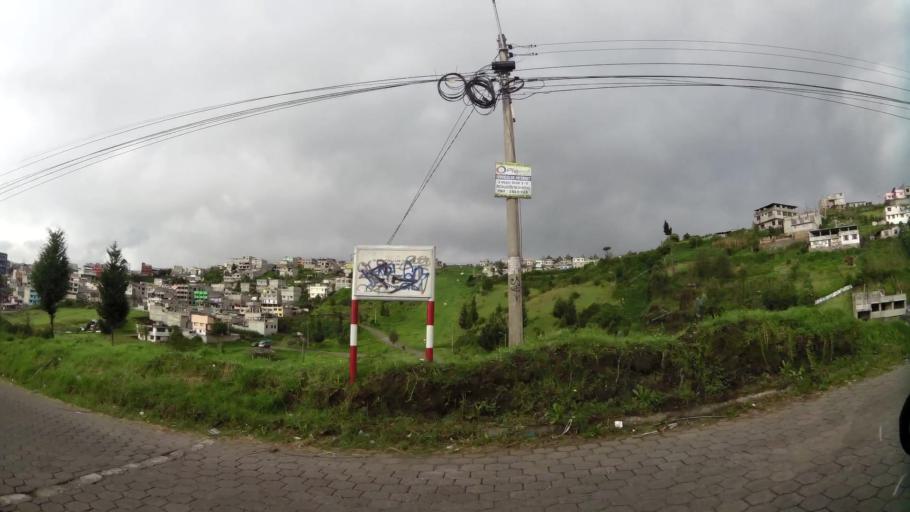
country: EC
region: Pichincha
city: Quito
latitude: -0.2962
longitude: -78.5243
